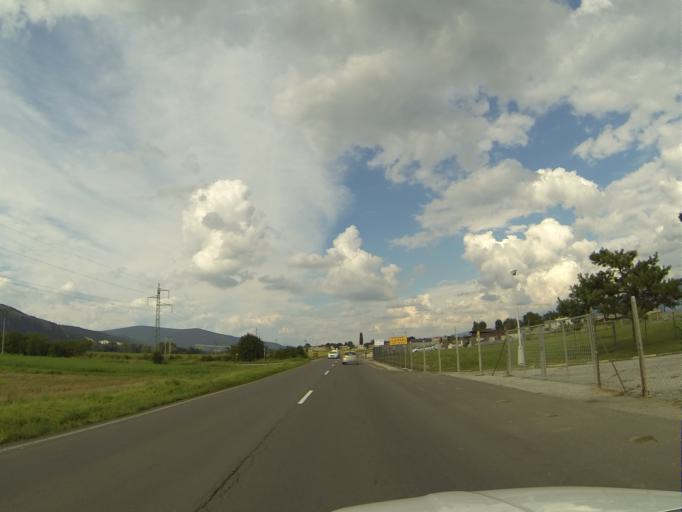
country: SK
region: Nitriansky
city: Partizanske
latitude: 48.6263
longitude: 18.4587
